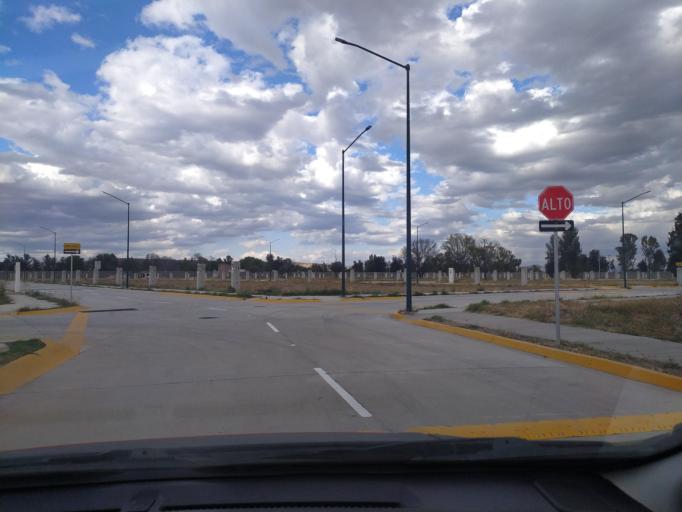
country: LA
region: Oudomxai
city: Muang La
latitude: 21.0244
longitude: 101.8221
